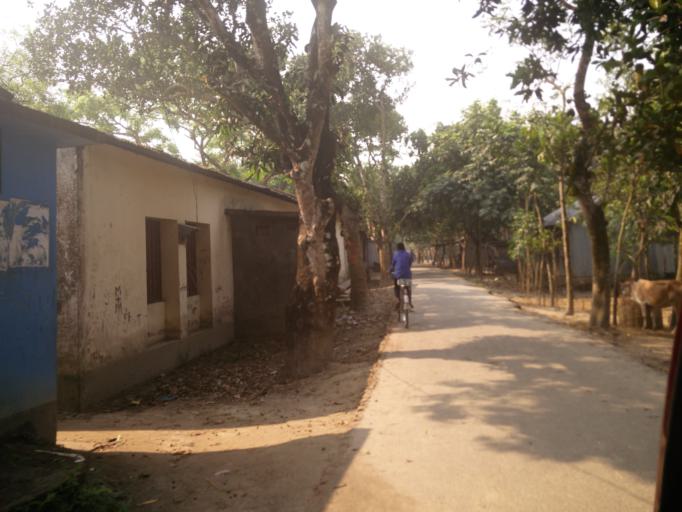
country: BD
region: Dhaka
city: Sherpur
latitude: 24.9125
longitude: 90.1560
